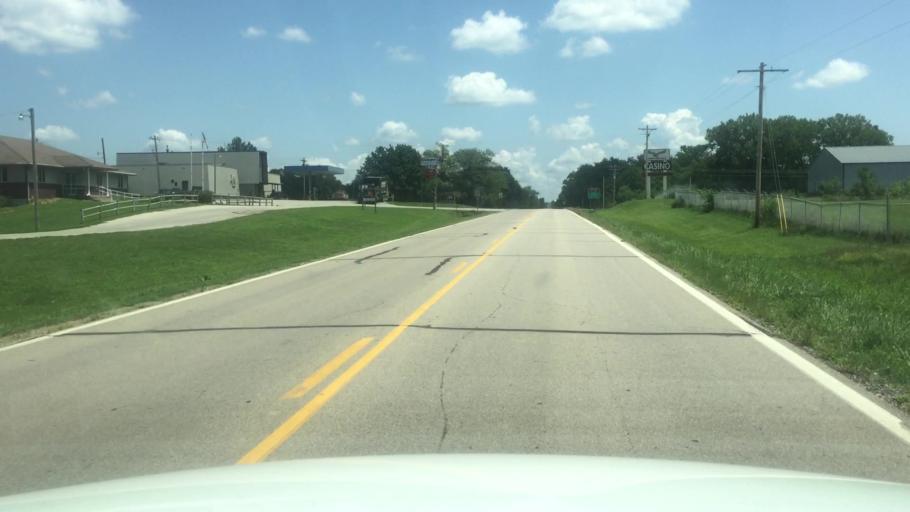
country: US
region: Kansas
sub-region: Brown County
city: Horton
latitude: 39.6674
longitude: -95.6414
